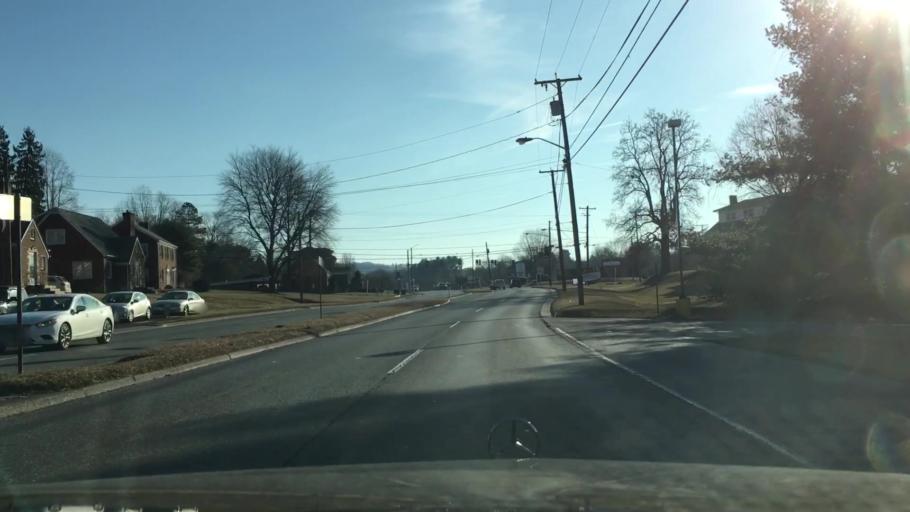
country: US
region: Virginia
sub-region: Roanoke County
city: Vinton
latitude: 37.2780
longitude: -79.8836
